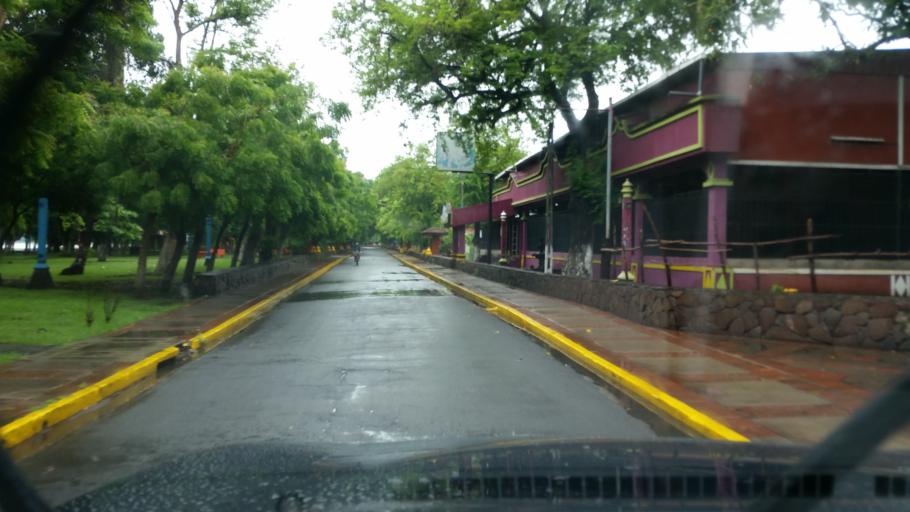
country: NI
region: Granada
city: Granada
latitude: 11.9258
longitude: -85.9414
